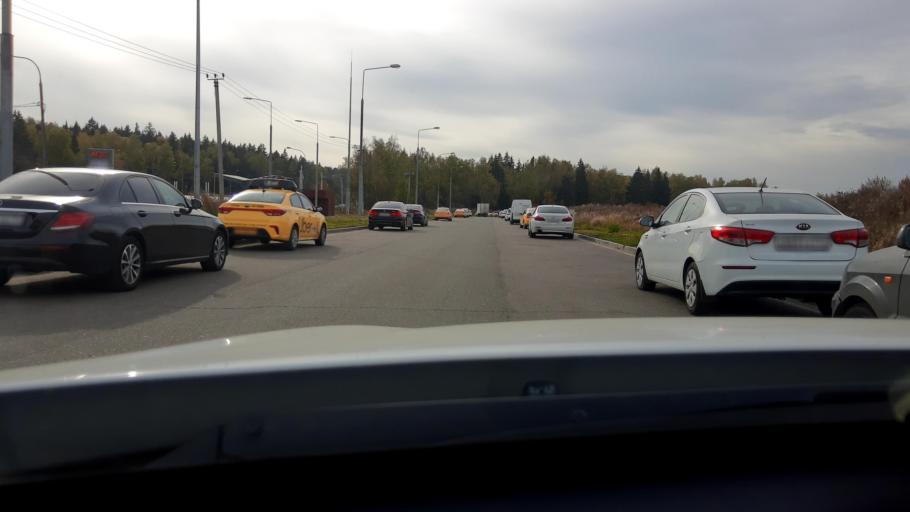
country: RU
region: Moskovskaya
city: Vostryakovo
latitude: 55.4652
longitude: 37.8526
